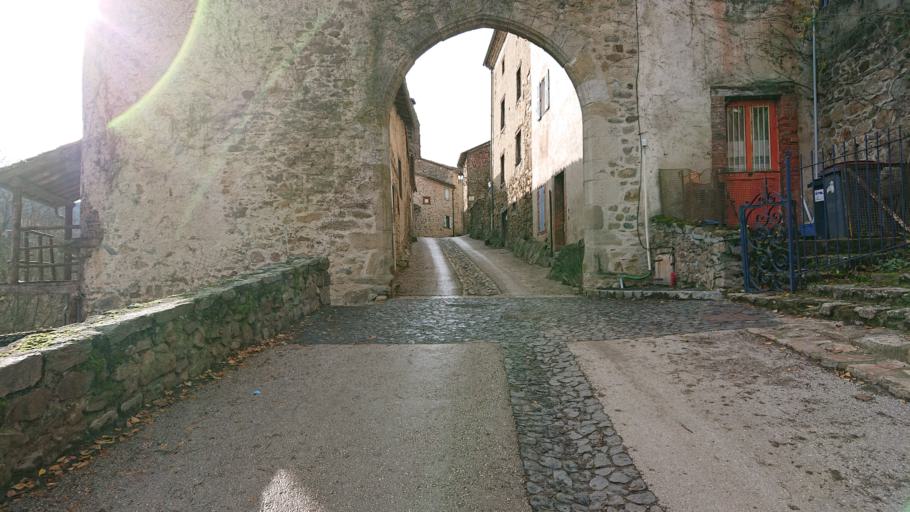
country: FR
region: Auvergne
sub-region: Departement de la Haute-Loire
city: Vieille-Brioude
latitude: 45.2632
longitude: 3.4553
